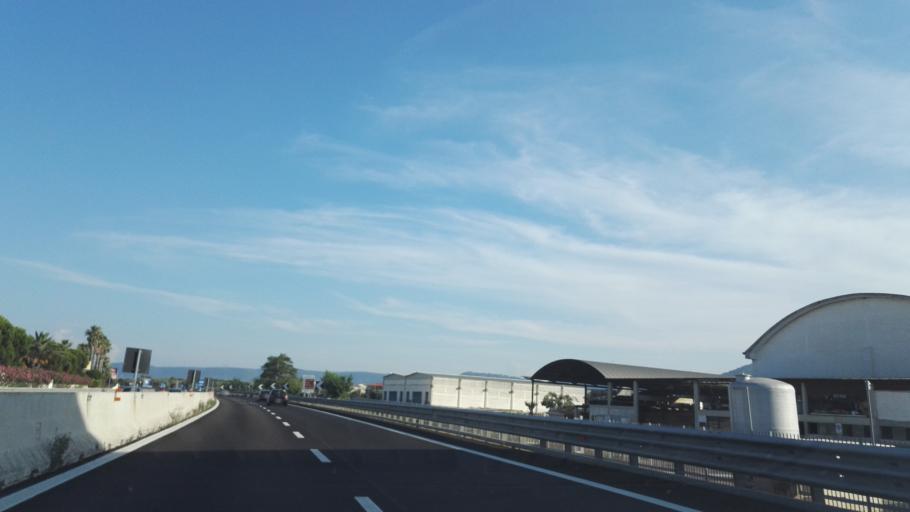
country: IT
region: Apulia
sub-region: Provincia di Brindisi
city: Fasano
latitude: 40.8598
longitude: 17.3488
